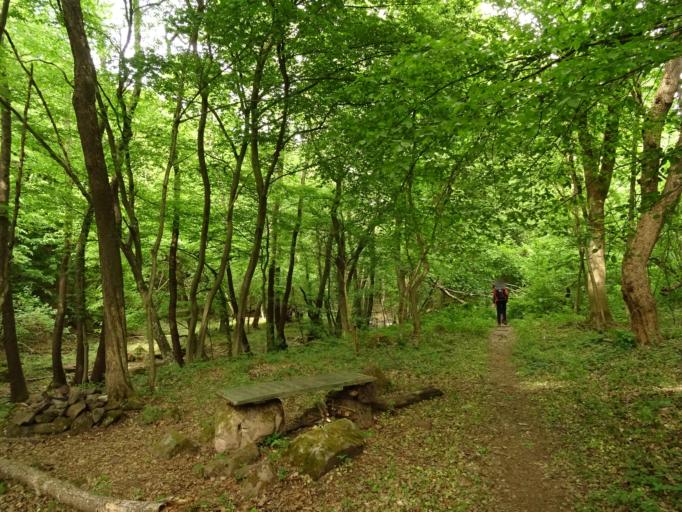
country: HU
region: Borsod-Abauj-Zemplen
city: Gonc
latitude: 48.3766
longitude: 21.2905
